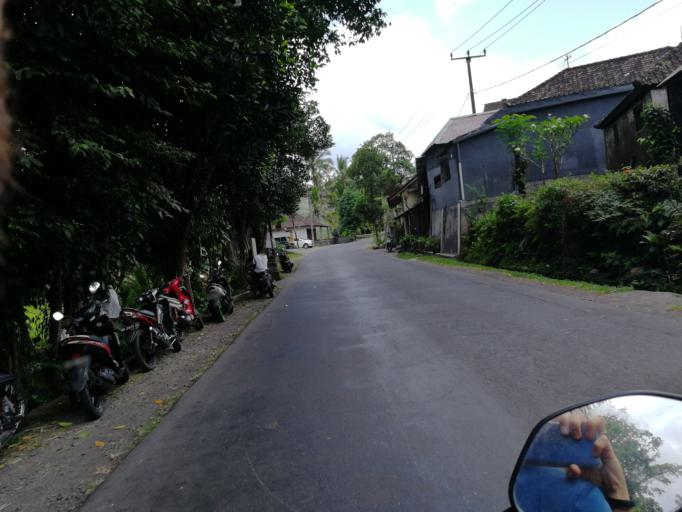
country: ID
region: Bali
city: Banjar Wangsian
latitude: -8.4606
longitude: 115.4489
